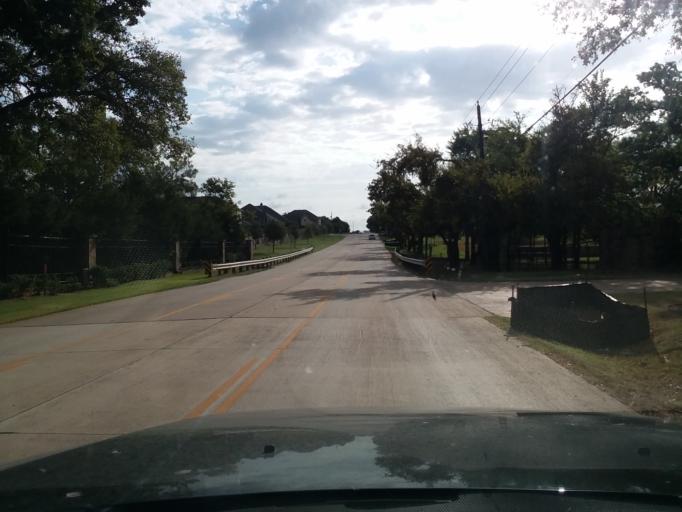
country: US
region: Texas
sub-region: Denton County
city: Hickory Creek
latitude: 33.1227
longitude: -97.0502
